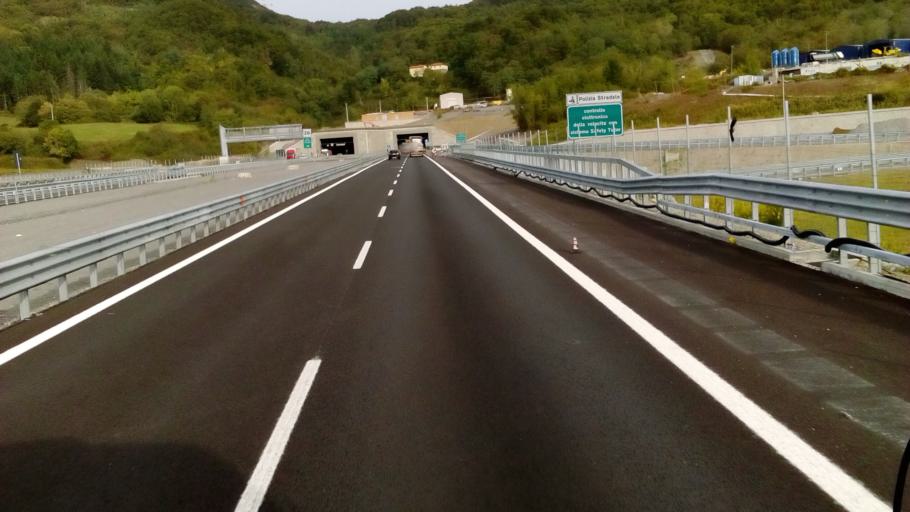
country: IT
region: Tuscany
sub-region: Province of Florence
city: Barberino di Mugello
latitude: 44.0702
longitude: 11.2407
